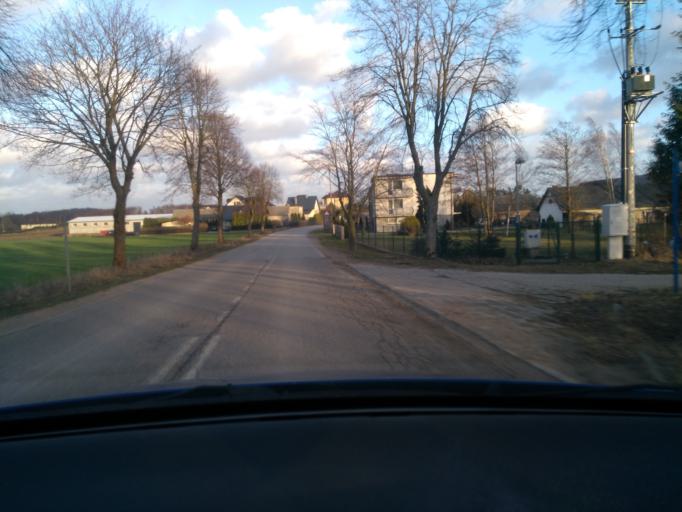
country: PL
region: Pomeranian Voivodeship
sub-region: Powiat kartuski
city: Przodkowo
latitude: 54.4158
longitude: 18.3065
